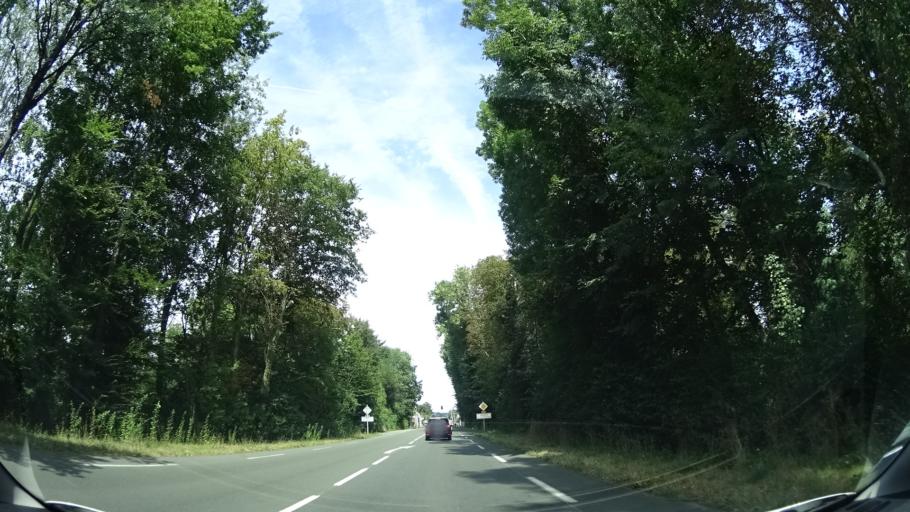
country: FR
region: Pays de la Loire
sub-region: Departement de la Sarthe
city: La Fleche
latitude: 47.7180
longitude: -0.1049
